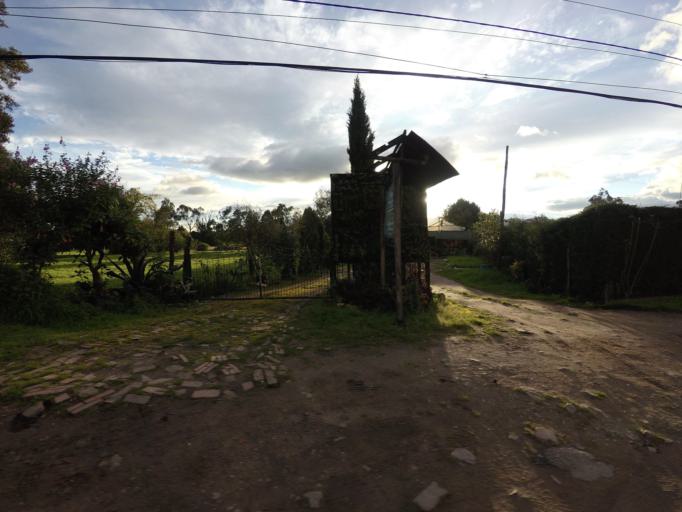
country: CO
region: Cundinamarca
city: Chia
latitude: 4.8162
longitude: -74.0307
